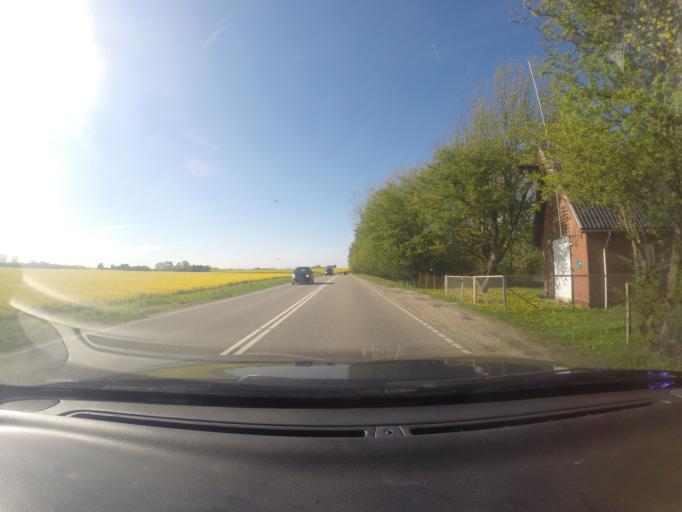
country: DK
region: Capital Region
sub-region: Hoje-Taastrup Kommune
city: Taastrup
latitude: 55.6679
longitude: 12.2767
